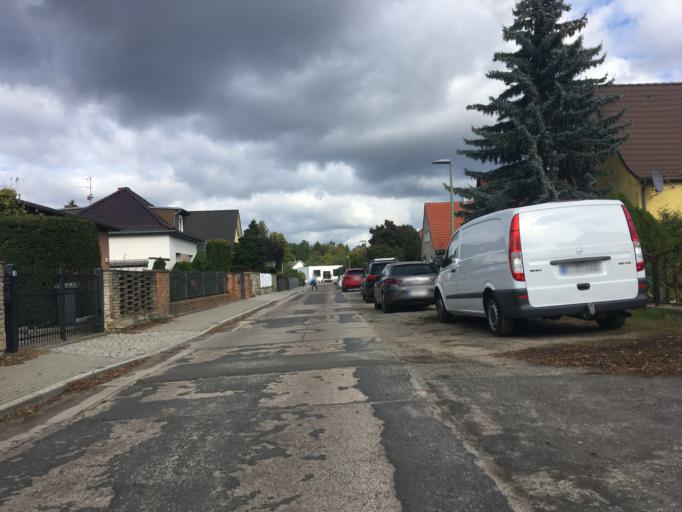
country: DE
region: Berlin
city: Baumschulenweg
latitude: 52.4501
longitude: 13.4827
